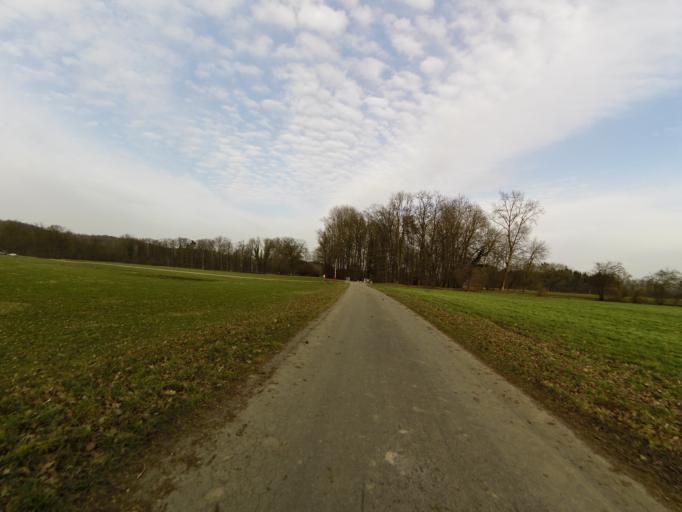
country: CH
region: Thurgau
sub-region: Frauenfeld District
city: Frauenfeld
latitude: 47.5790
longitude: 8.9155
